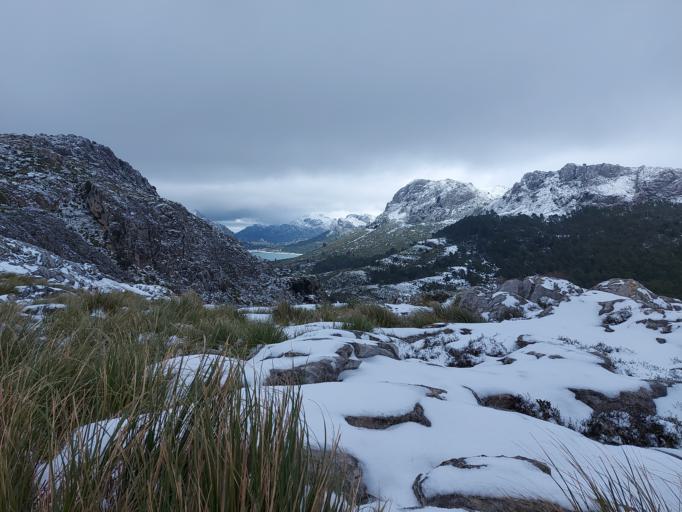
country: ES
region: Balearic Islands
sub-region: Illes Balears
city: Fornalutx
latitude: 39.7680
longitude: 2.7623
